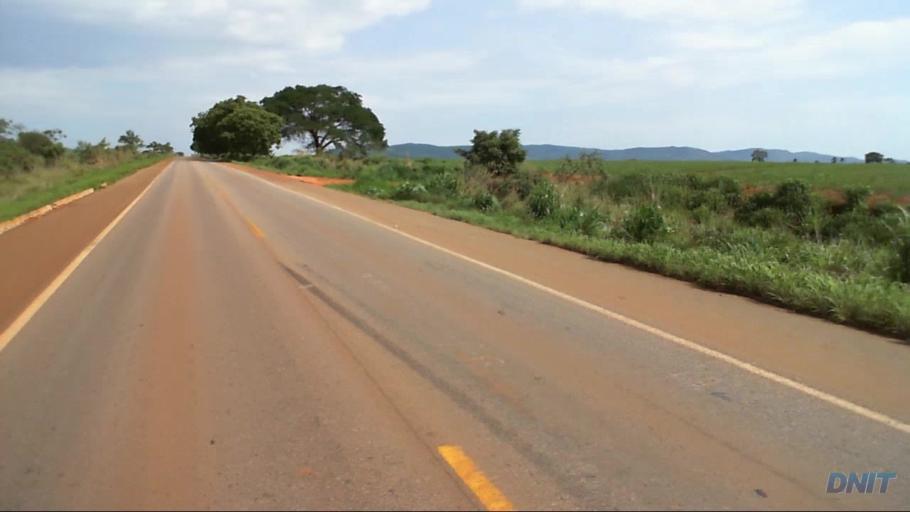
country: BR
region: Goias
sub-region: Barro Alto
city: Barro Alto
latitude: -15.0400
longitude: -48.8903
